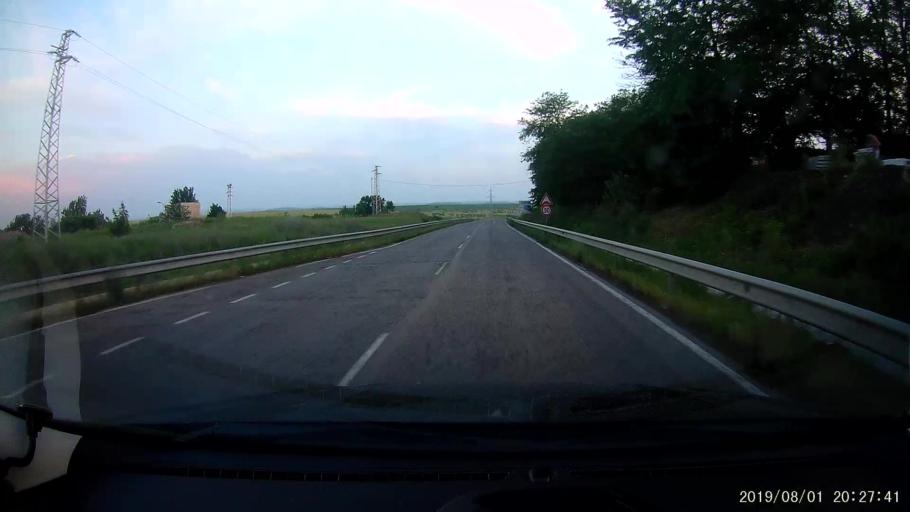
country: BG
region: Yambol
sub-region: Obshtina Elkhovo
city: Elkhovo
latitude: 42.1759
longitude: 26.5838
